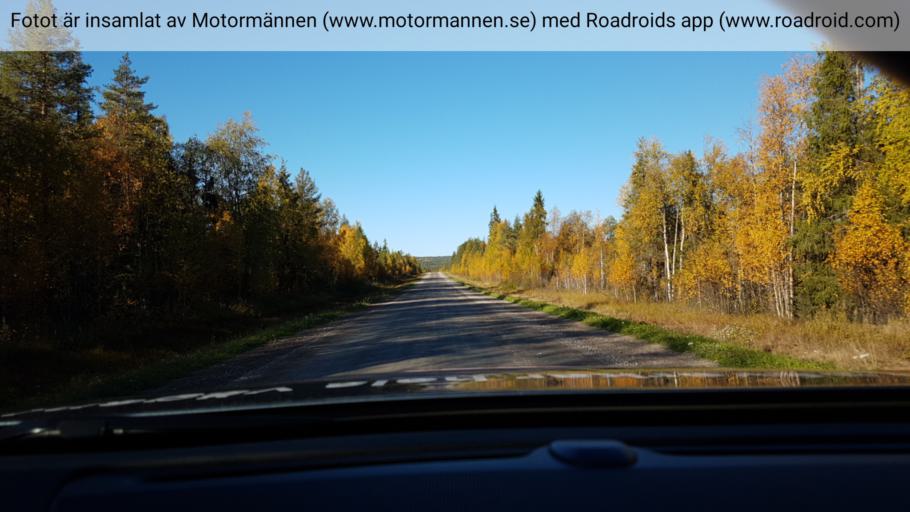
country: SE
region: Norrbotten
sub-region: Alvsbyns Kommun
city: AElvsbyn
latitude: 66.2650
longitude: 21.0360
